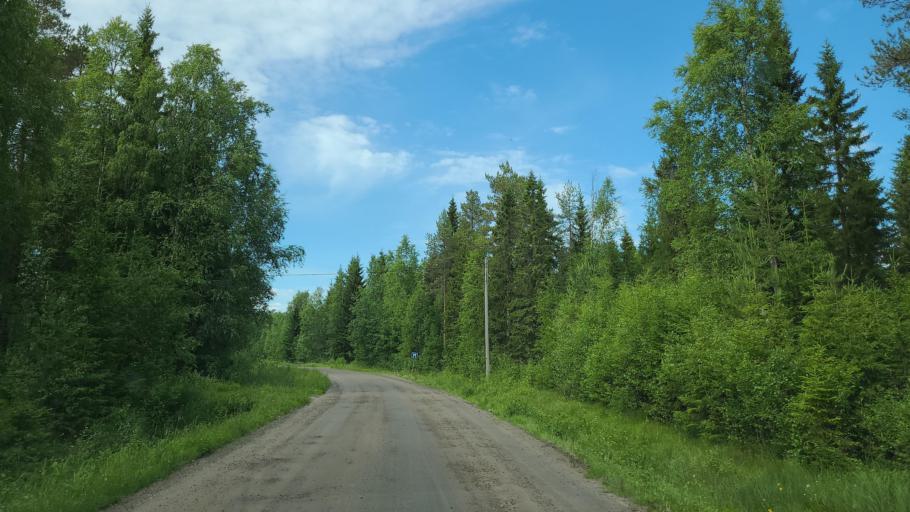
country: SE
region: Vaesterbotten
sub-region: Robertsfors Kommun
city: Robertsfors
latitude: 64.1646
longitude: 20.9702
